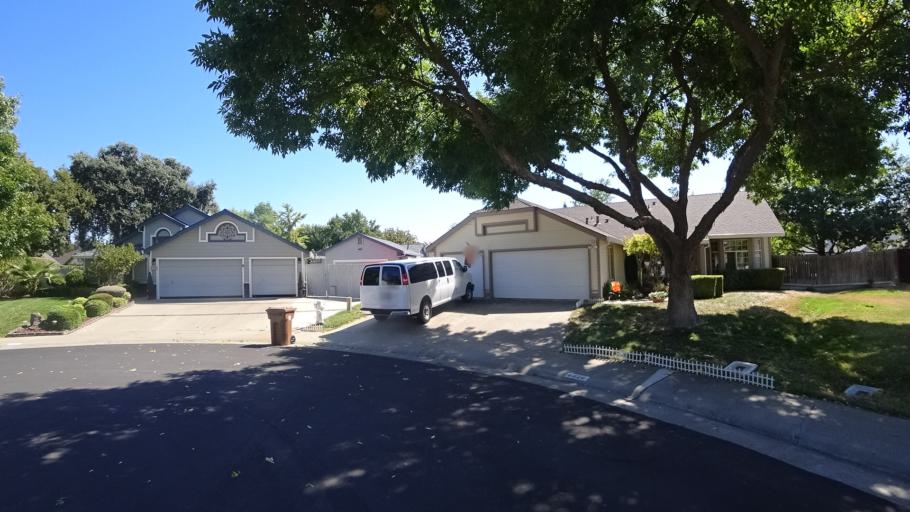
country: US
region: California
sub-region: Sacramento County
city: Laguna
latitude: 38.4334
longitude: -121.4327
